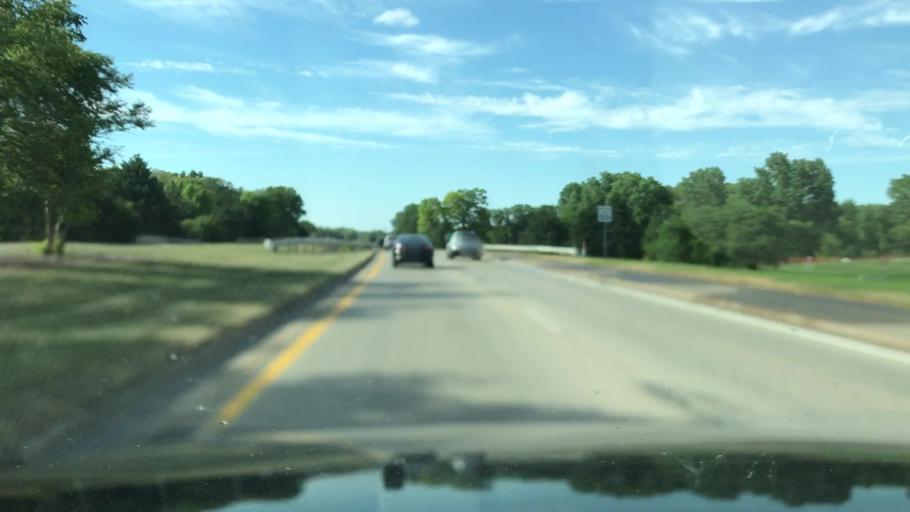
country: US
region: Michigan
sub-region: Kent County
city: East Grand Rapids
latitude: 42.9306
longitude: -85.5845
